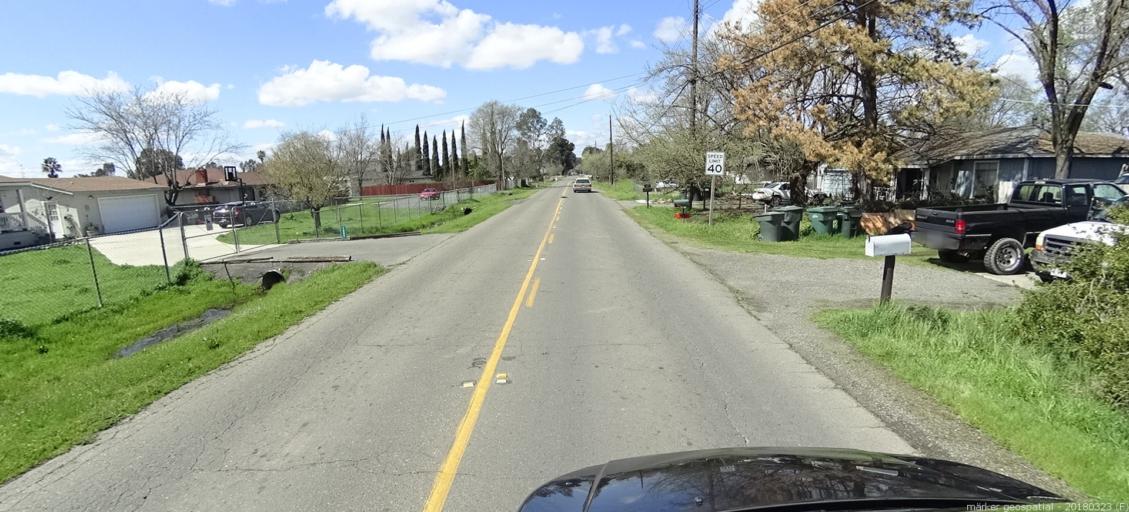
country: US
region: California
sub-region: Sacramento County
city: Rio Linda
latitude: 38.6763
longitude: -121.4203
